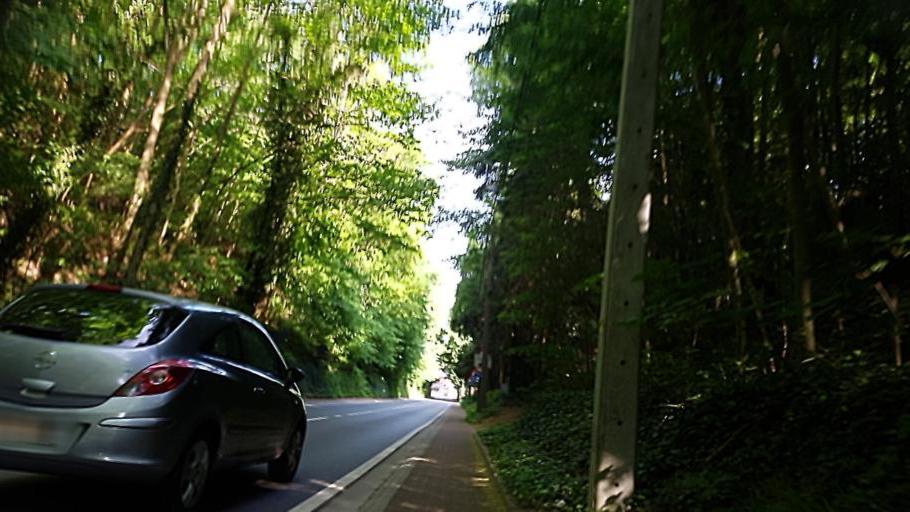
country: BE
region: Flanders
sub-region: Provincie Vlaams-Brabant
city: Overijse
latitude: 50.7699
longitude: 4.5453
